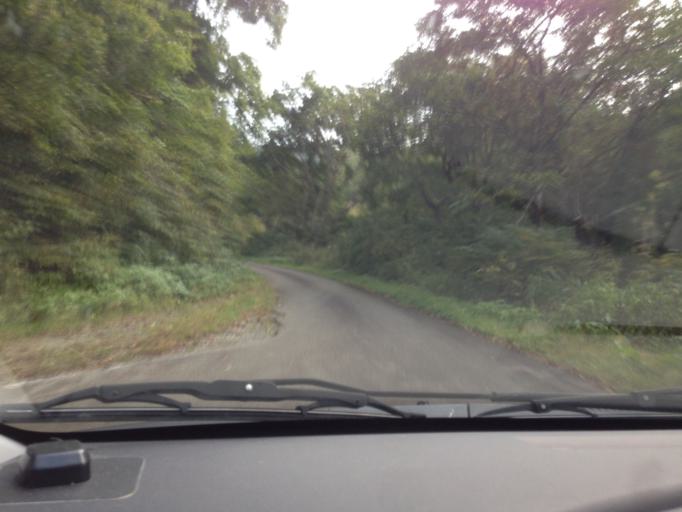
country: JP
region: Fukushima
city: Kitakata
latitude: 37.3858
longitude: 139.6148
